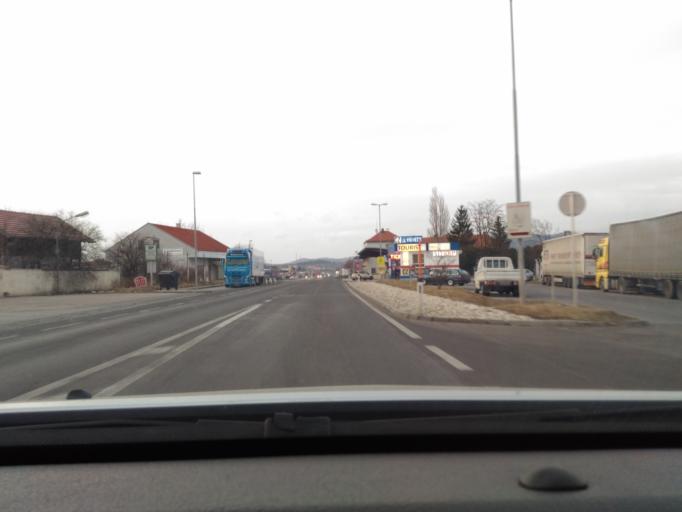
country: CZ
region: South Moravian
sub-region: Okres Breclav
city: Mikulov
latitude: 48.7775
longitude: 16.6410
